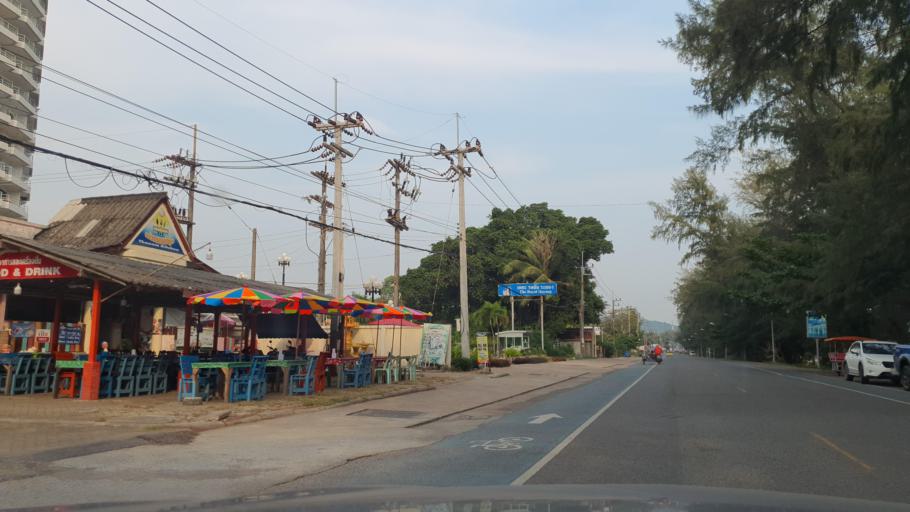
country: TH
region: Rayong
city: Rayong
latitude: 12.6029
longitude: 101.4000
